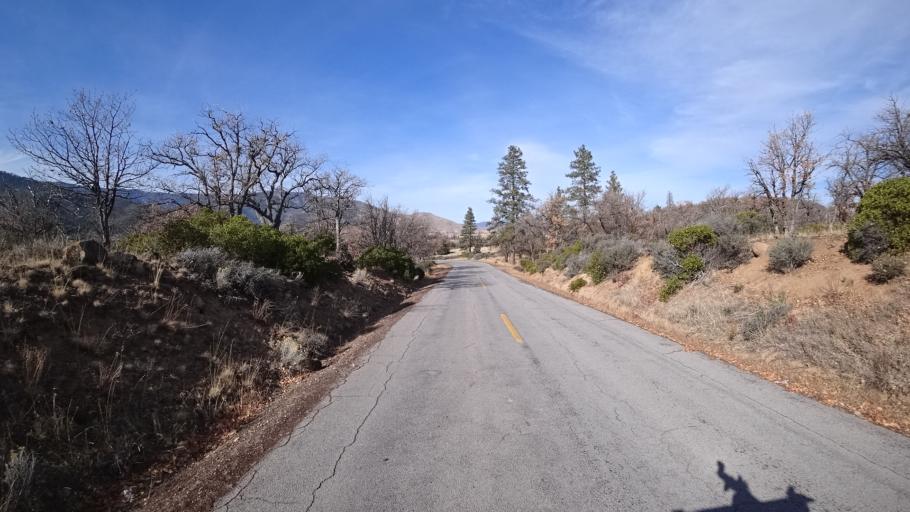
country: US
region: California
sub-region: Siskiyou County
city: Weed
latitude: 41.4319
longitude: -122.4265
